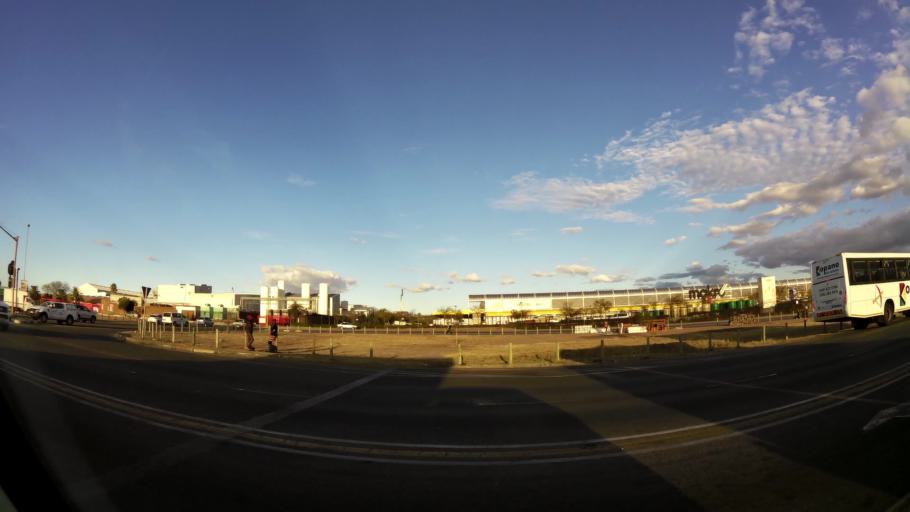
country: ZA
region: Limpopo
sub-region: Capricorn District Municipality
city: Polokwane
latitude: -23.8733
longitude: 29.4637
